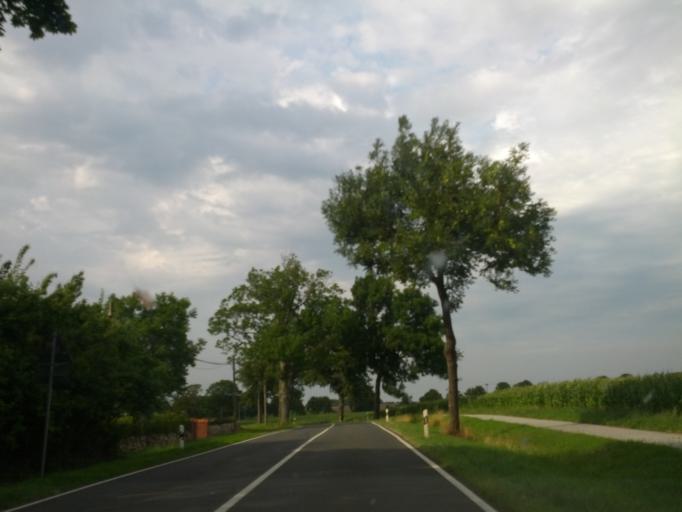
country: DE
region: Mecklenburg-Vorpommern
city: Kropelin
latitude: 54.0533
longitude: 11.7996
